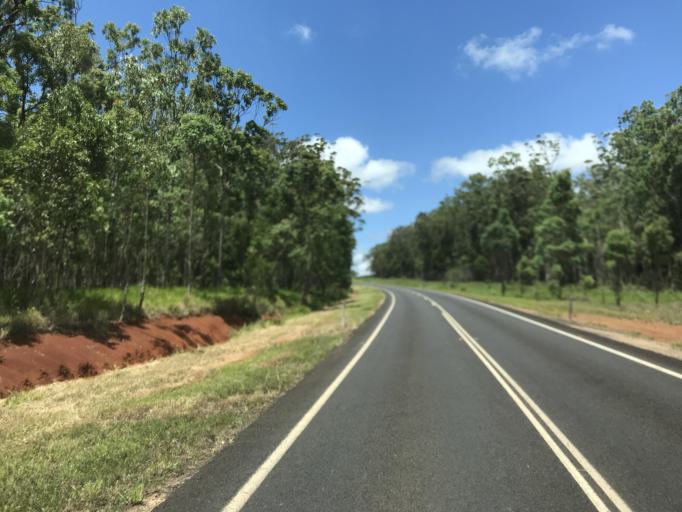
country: AU
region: Queensland
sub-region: Tablelands
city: Ravenshoe
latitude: -17.5366
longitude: 145.4516
